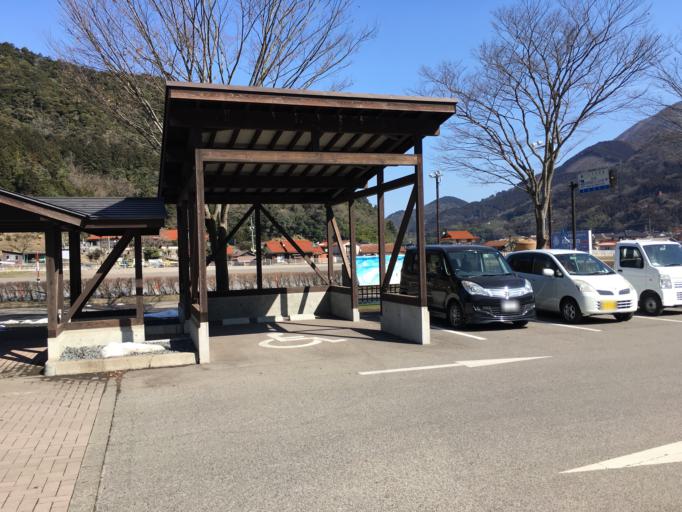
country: JP
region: Shimane
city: Masuda
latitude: 34.4508
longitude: 131.7601
